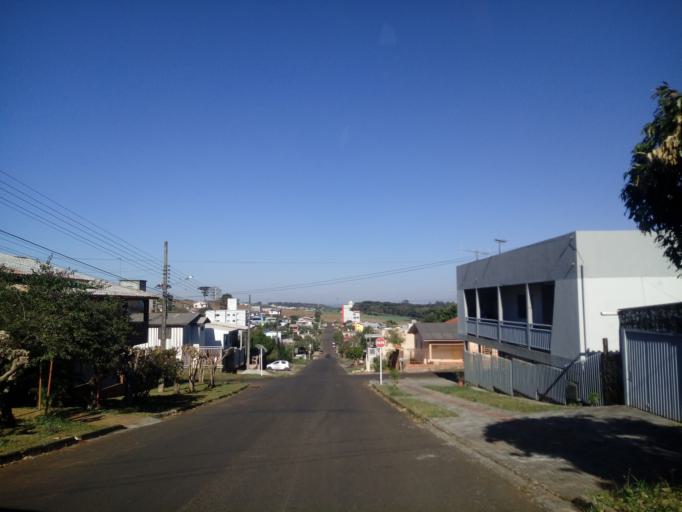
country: BR
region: Santa Catarina
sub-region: Chapeco
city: Chapeco
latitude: -27.0788
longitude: -52.6336
